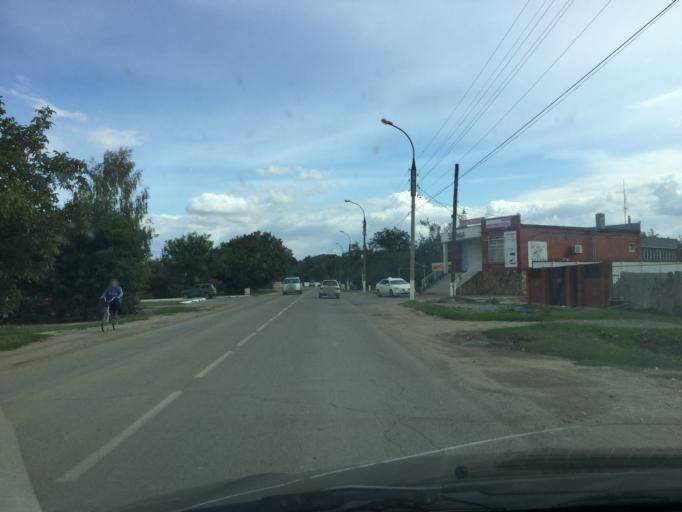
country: RU
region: Krasnodarskiy
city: Sovkhoznyy
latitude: 45.2852
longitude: 38.1034
